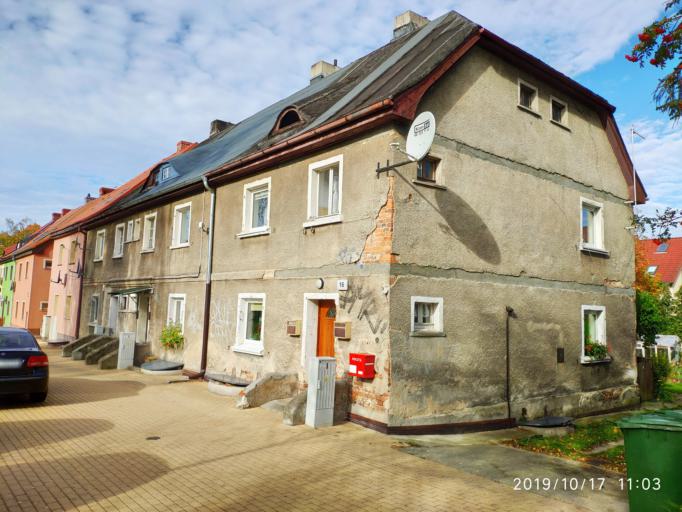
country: PL
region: Lubusz
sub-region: Zielona Gora
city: Zielona Gora
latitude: 51.9392
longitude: 15.5356
